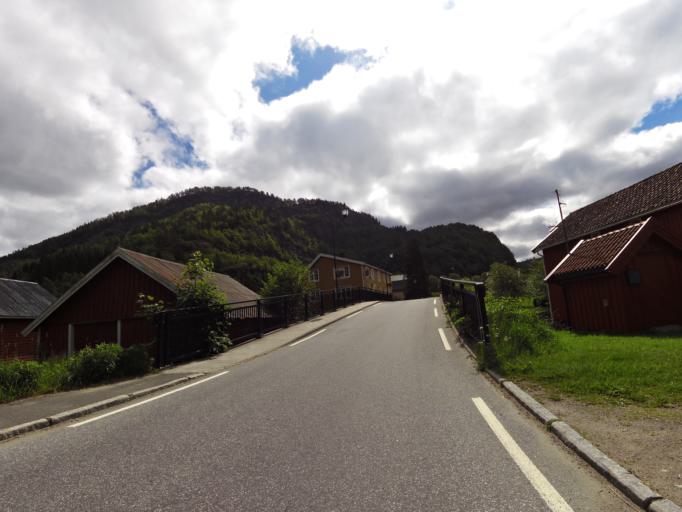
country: NO
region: Vest-Agder
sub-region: Kvinesdal
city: Liknes
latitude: 58.2710
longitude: 6.8145
